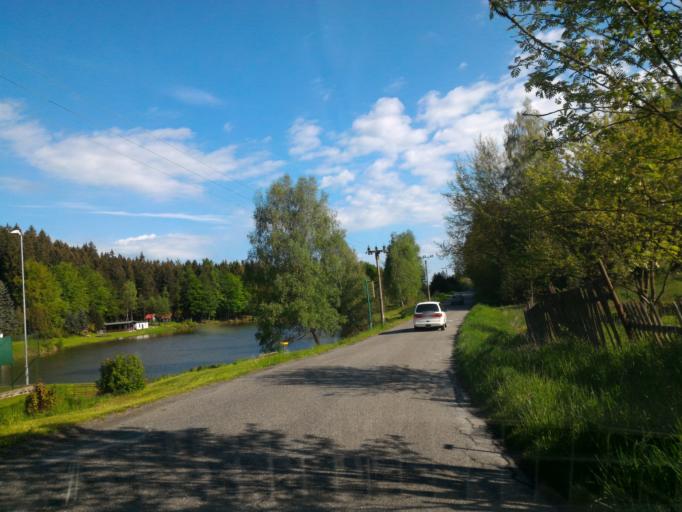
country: CZ
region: Vysocina
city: Ledec nad Sazavou
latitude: 49.6381
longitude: 15.3004
